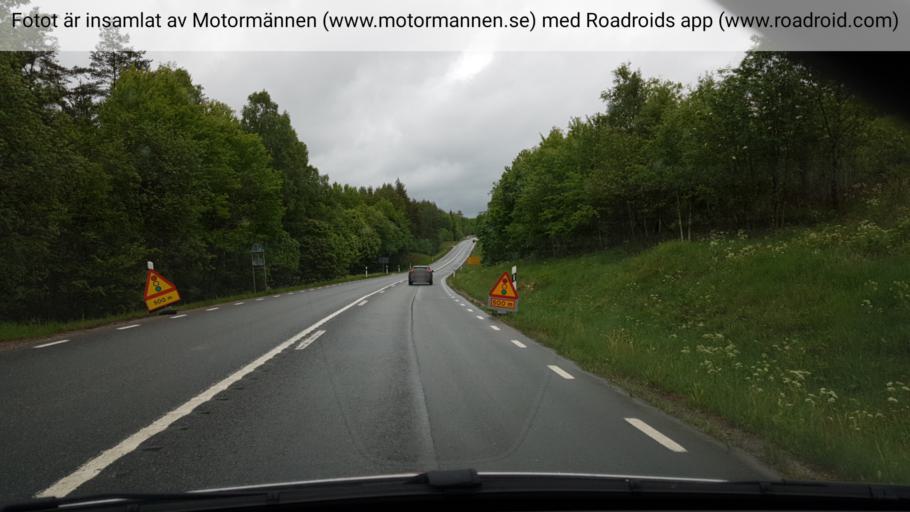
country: SE
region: Joenkoeping
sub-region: Aneby Kommun
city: Aneby
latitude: 57.9035
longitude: 14.8930
